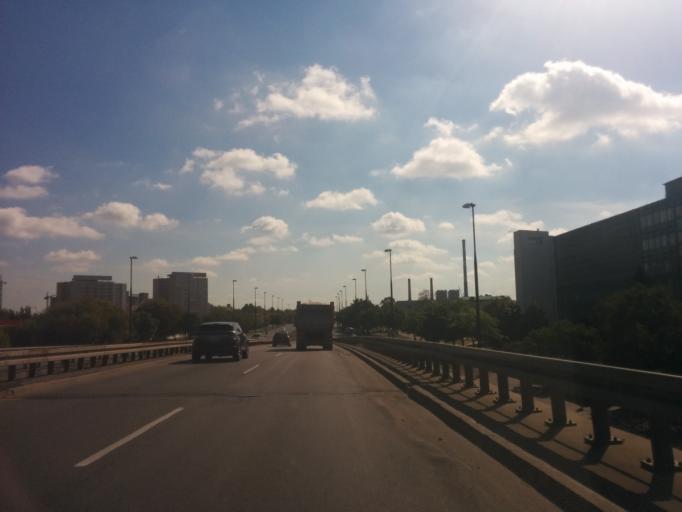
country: PL
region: Masovian Voivodeship
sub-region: Warszawa
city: Bialoleka
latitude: 52.3078
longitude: 20.9835
